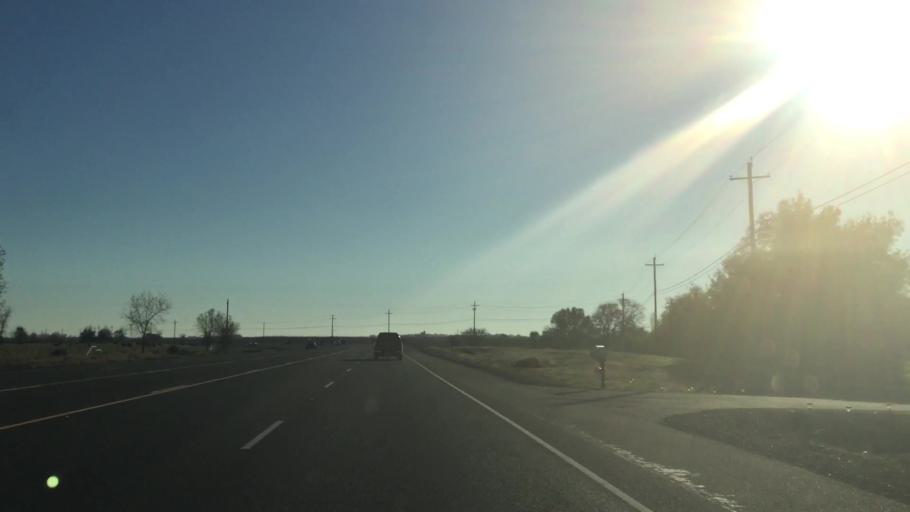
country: US
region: California
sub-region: Butte County
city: Gridley
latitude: 39.3812
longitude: -121.6126
